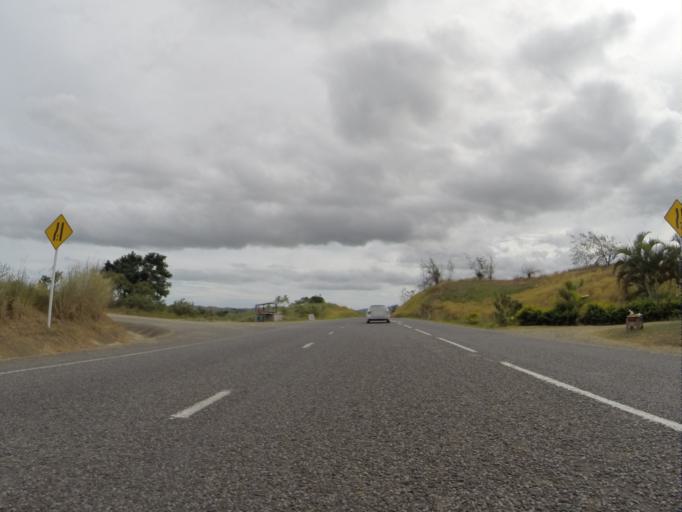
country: FJ
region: Western
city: Nadi
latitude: -18.0324
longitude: 177.3330
